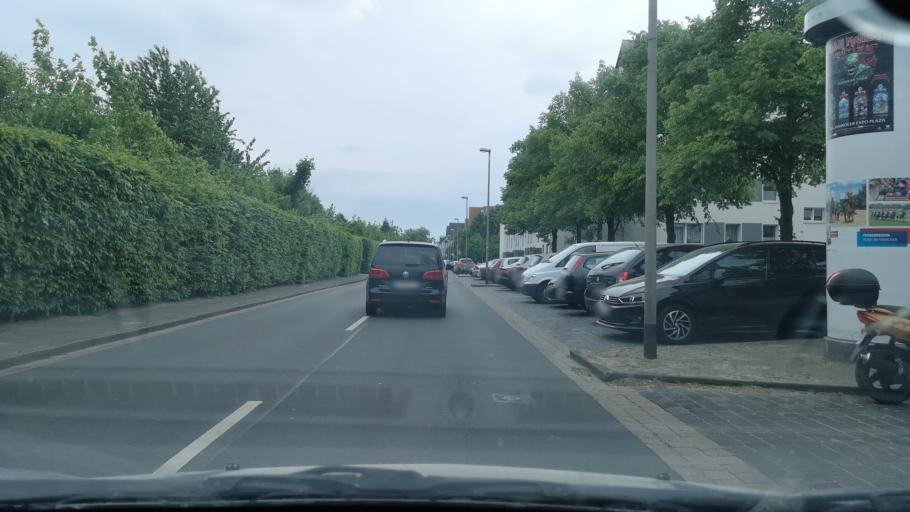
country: DE
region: Lower Saxony
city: Hannover
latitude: 52.4071
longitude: 9.6952
